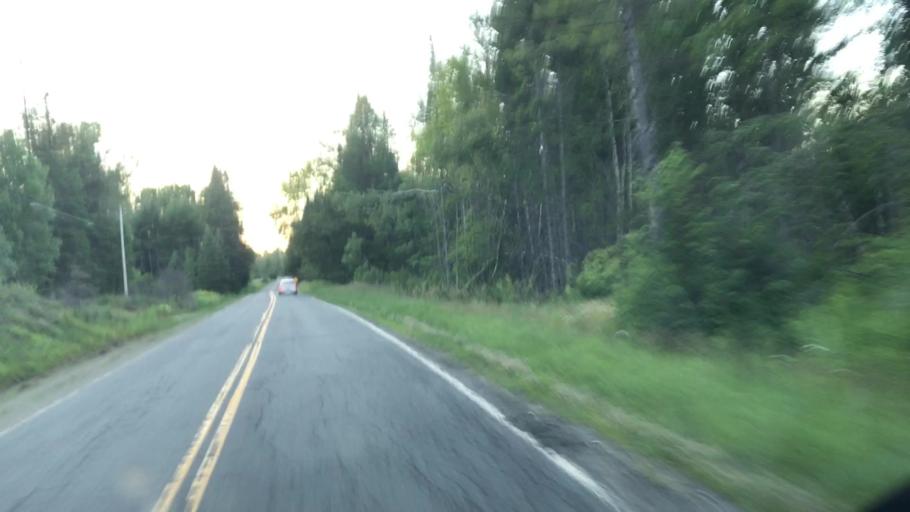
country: US
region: Maine
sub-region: Penobscot County
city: Medway
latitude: 45.6089
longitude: -68.2571
